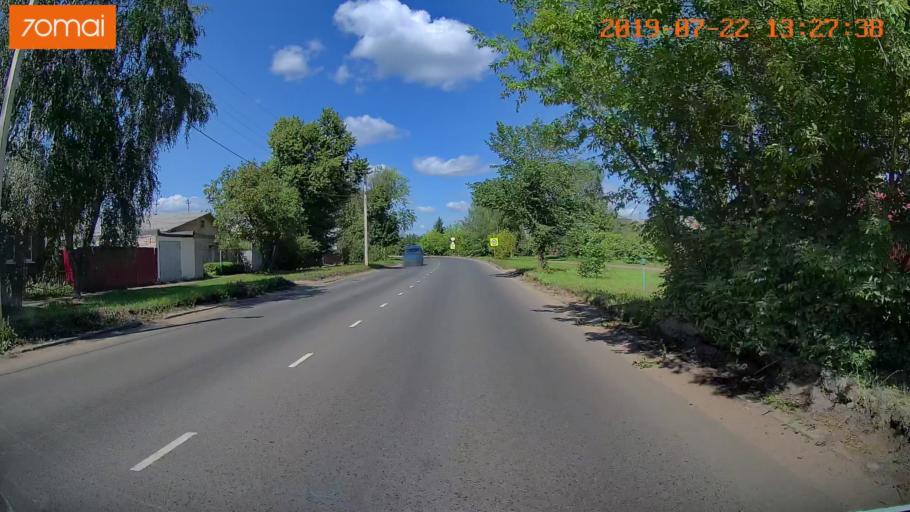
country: RU
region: Ivanovo
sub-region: Gorod Ivanovo
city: Ivanovo
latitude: 57.0368
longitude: 40.9506
